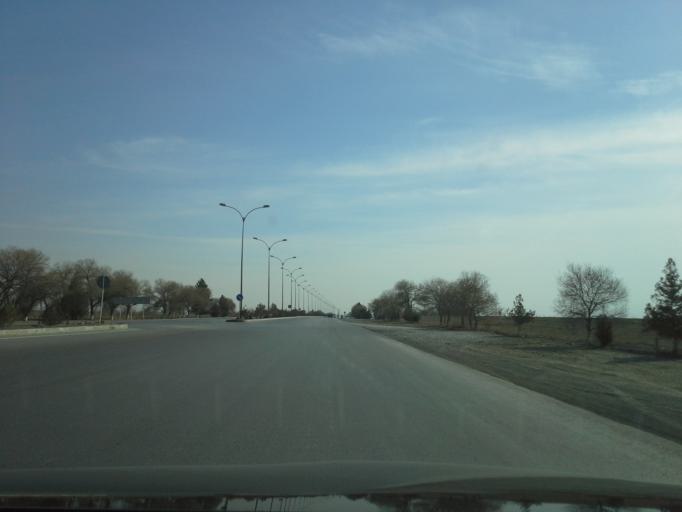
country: TM
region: Ahal
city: Abadan
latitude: 38.1247
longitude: 58.0346
